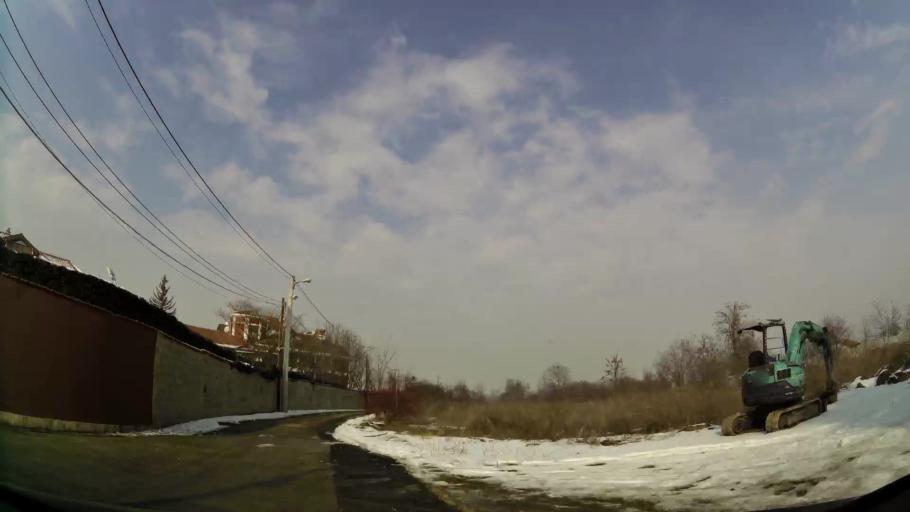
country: MK
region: Suto Orizari
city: Suto Orizare
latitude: 42.0169
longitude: 21.3862
